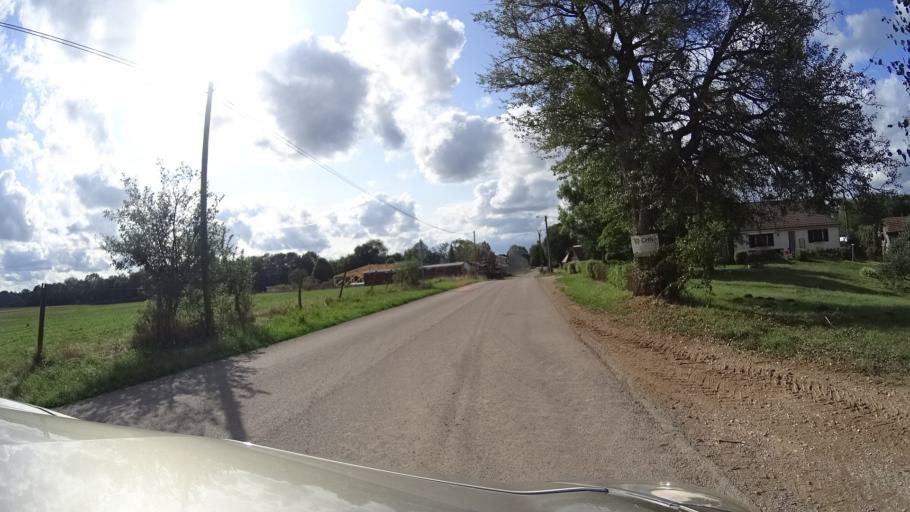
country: FR
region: Franche-Comte
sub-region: Departement du Doubs
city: Mamirolle
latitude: 47.2065
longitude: 6.1472
